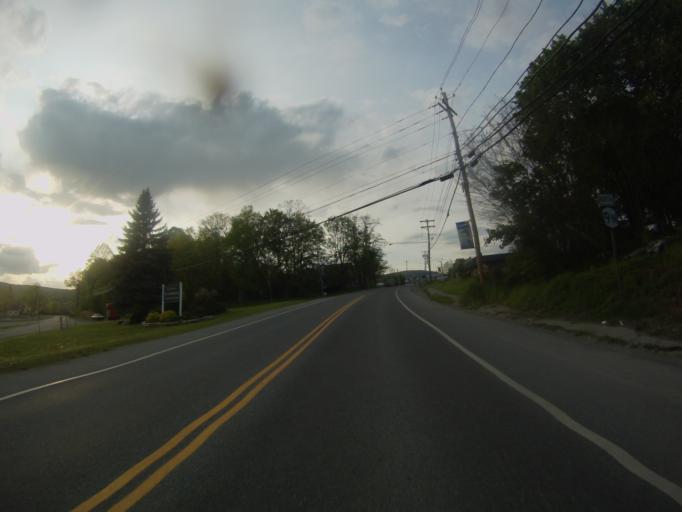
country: US
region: New York
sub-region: Essex County
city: Ticonderoga
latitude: 43.8528
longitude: -73.4374
